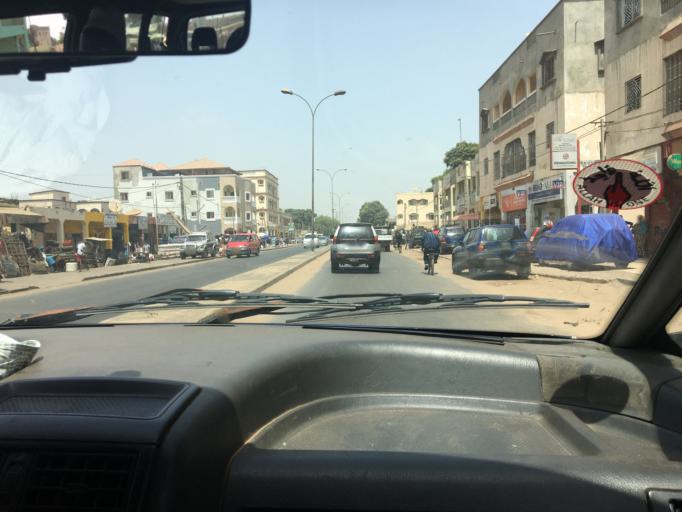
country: GM
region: Western
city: Abuko
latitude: 13.4072
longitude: -16.6663
